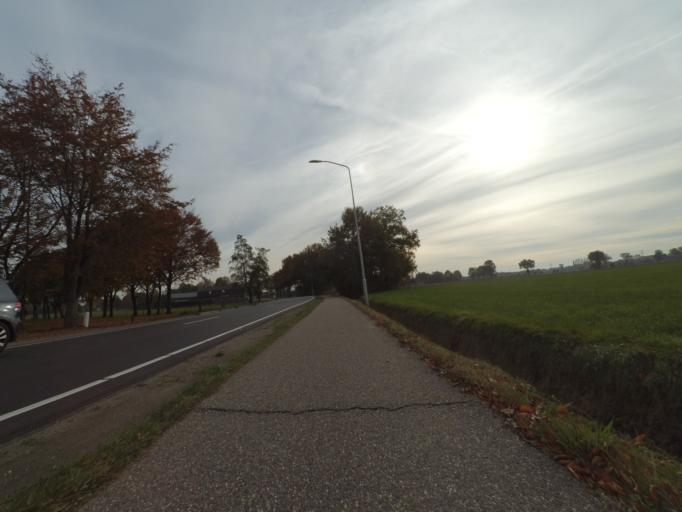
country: NL
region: Gelderland
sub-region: Gemeente Ede
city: Lunteren
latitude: 52.1092
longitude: 5.6004
